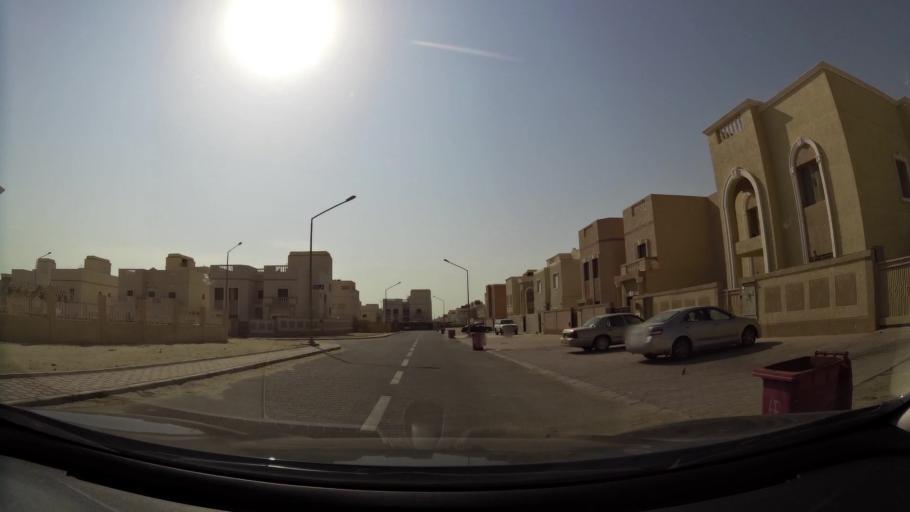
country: KW
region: Al Ahmadi
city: Al Wafrah
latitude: 28.7961
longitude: 48.0656
